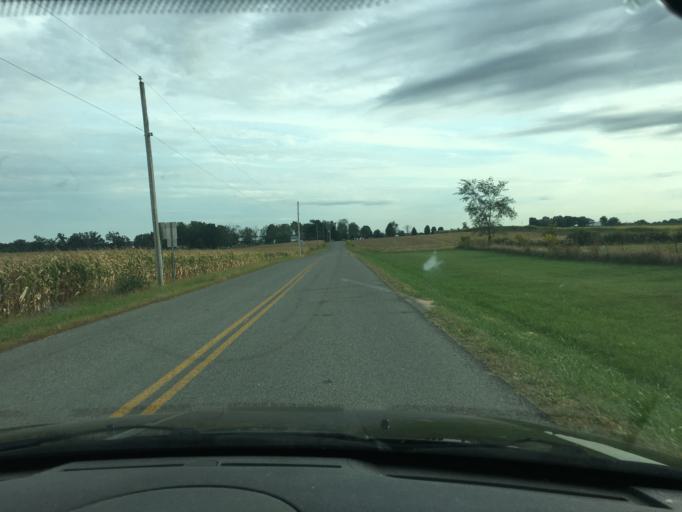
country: US
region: Ohio
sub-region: Logan County
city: West Liberty
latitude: 40.2955
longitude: -83.6847
